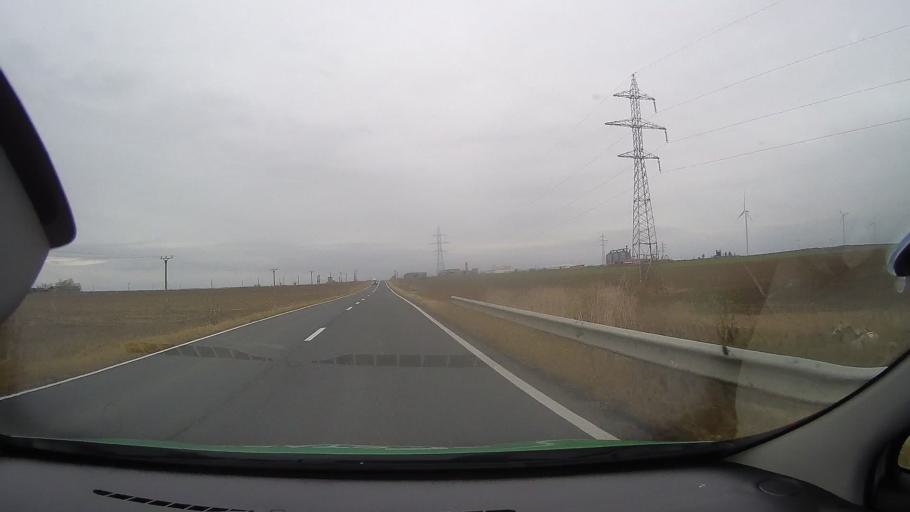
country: RO
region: Constanta
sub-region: Comuna Nicolae Balcescu
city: Dorobantu
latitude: 44.4258
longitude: 28.3088
